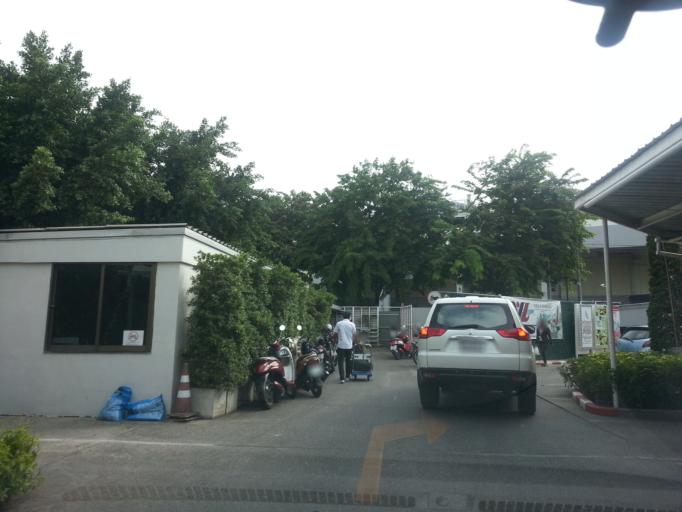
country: TH
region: Bangkok
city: Khlong Toei
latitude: 13.7197
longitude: 100.5696
